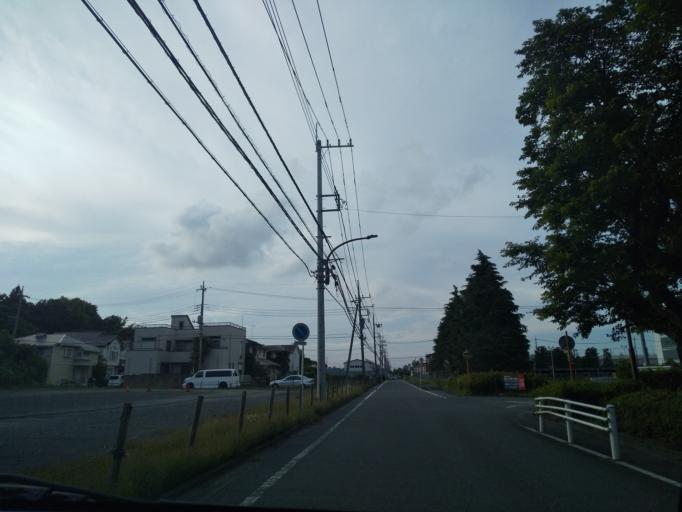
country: JP
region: Kanagawa
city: Zama
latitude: 35.5310
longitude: 139.3925
